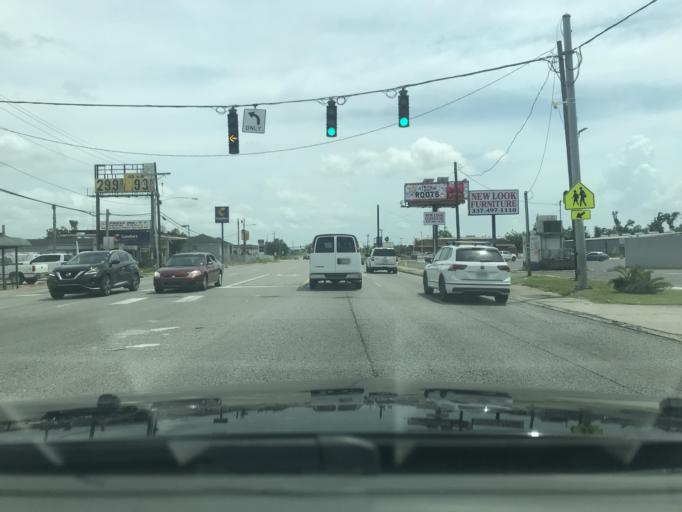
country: US
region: Louisiana
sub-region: Calcasieu Parish
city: Lake Charles
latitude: 30.2519
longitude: -93.1806
